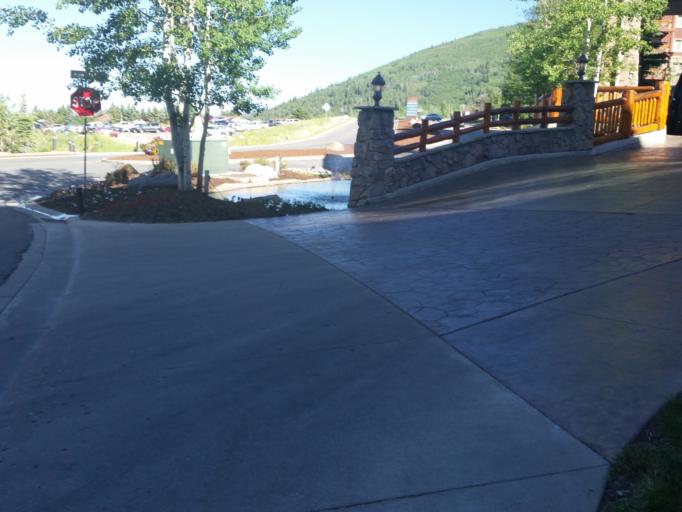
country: US
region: Utah
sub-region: Summit County
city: Snyderville
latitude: 40.6849
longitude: -111.5547
